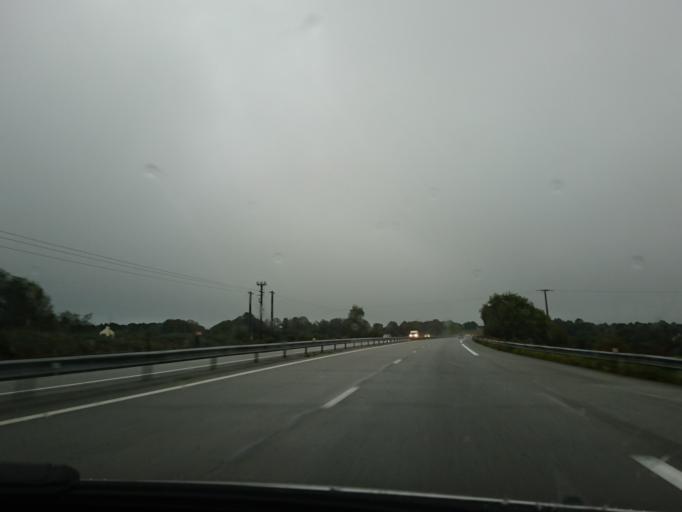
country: FR
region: Brittany
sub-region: Departement du Finistere
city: Briec
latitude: 48.1253
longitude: -4.0226
